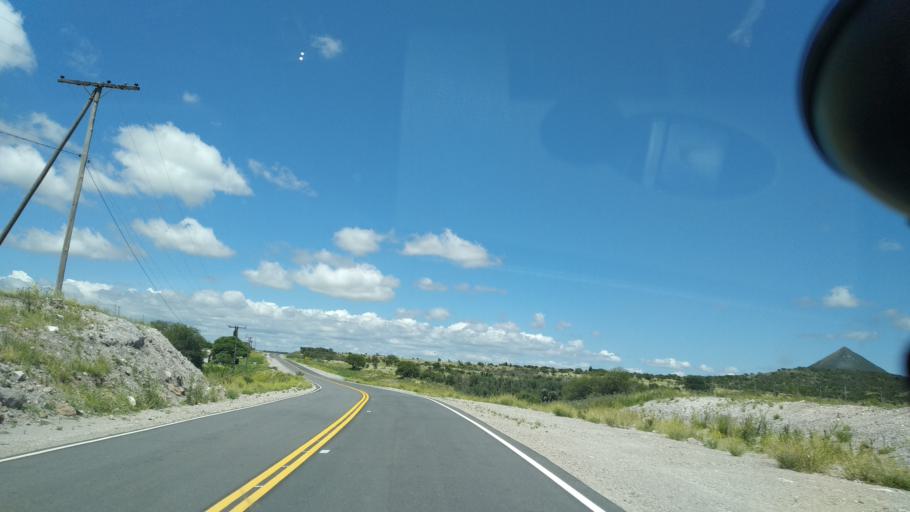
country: AR
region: Cordoba
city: Salsacate
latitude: -31.3486
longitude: -65.1140
